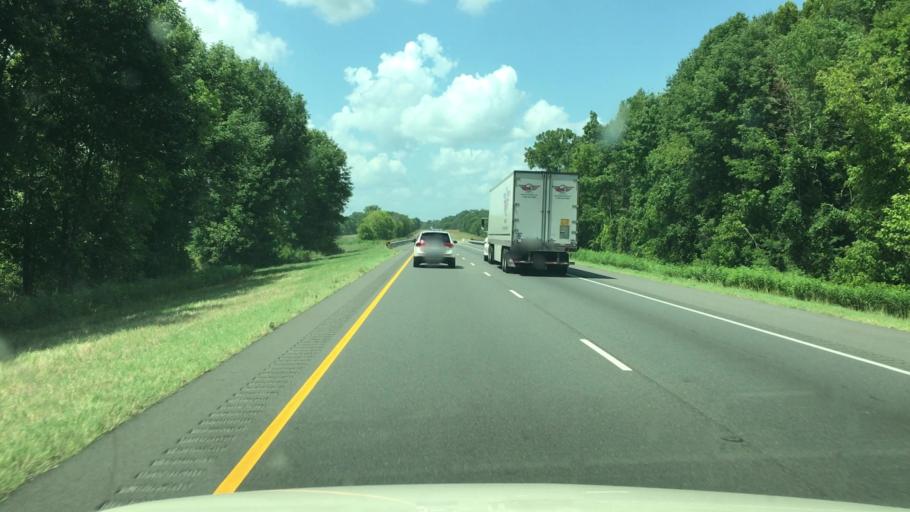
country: US
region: Arkansas
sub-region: Hempstead County
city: Hope
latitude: 33.7267
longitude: -93.5437
